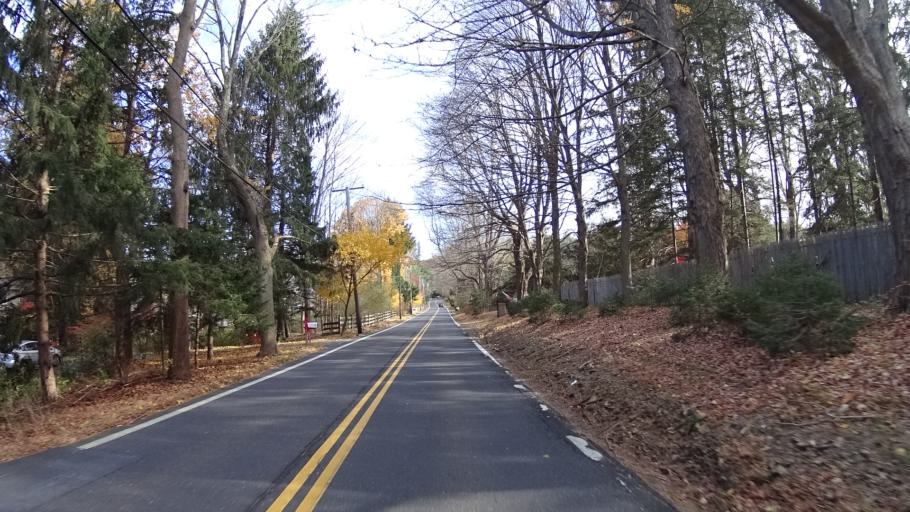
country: US
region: New Jersey
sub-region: Morris County
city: Mendham
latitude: 40.7701
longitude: -74.5663
